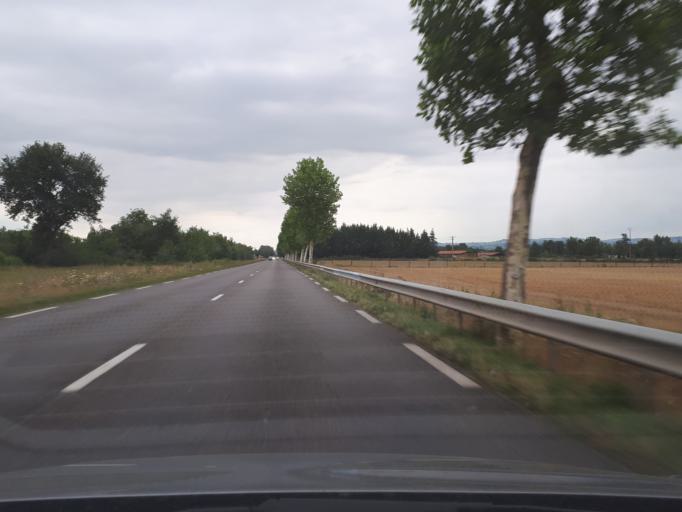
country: FR
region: Rhone-Alpes
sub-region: Departement de la Loire
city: Feurs
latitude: 45.7008
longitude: 4.2274
